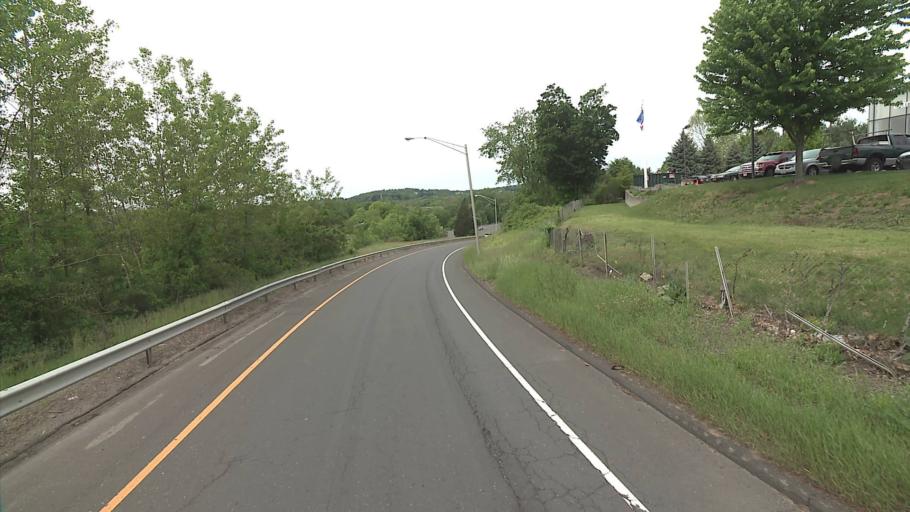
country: US
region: Connecticut
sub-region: Fairfield County
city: Bethel
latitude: 41.4143
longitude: -73.4104
